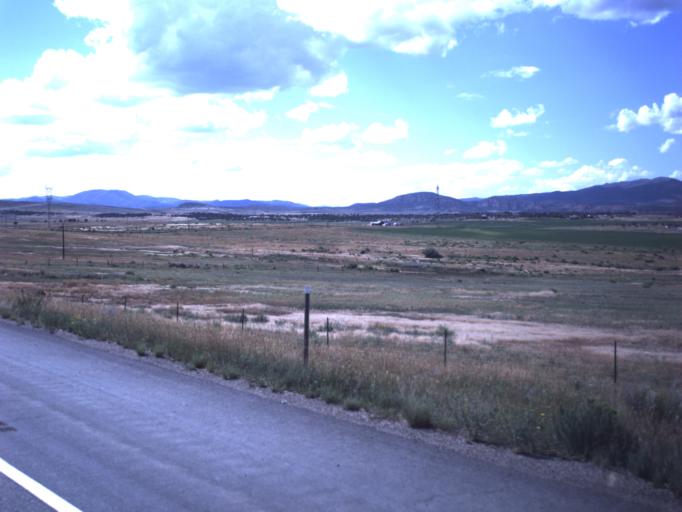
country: US
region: Utah
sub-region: Duchesne County
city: Duchesne
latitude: 40.2124
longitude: -110.8523
